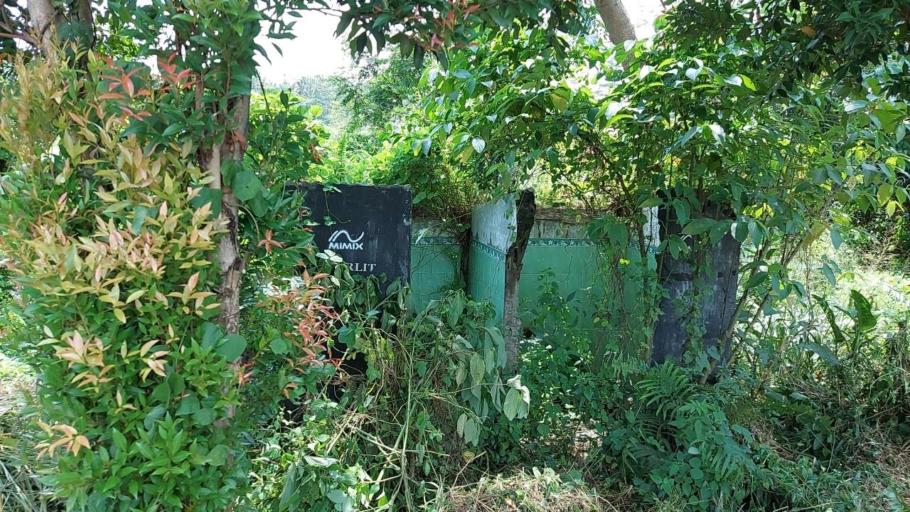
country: ID
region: West Java
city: Cibinong
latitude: -6.4900
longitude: 106.8513
